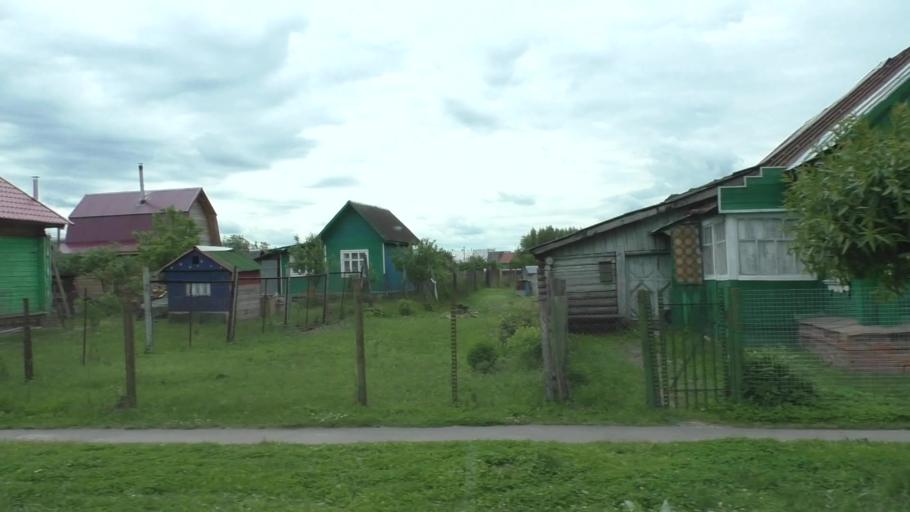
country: RU
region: Moskovskaya
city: Imeni Tsyurupy
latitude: 55.5054
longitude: 38.7753
